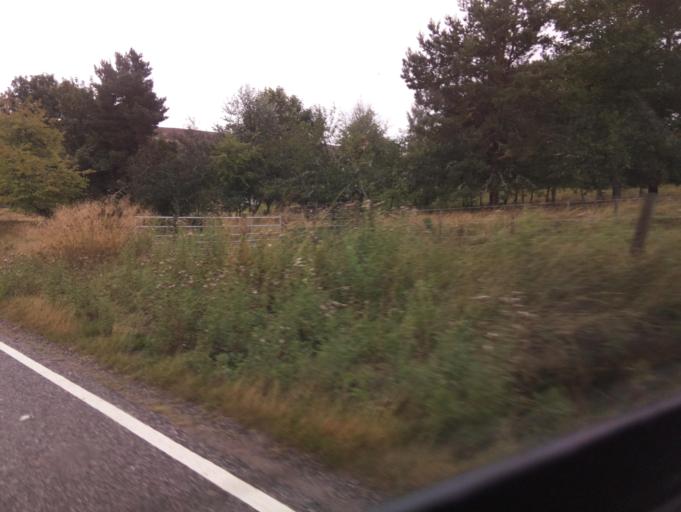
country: GB
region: Scotland
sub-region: Highland
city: Grantown on Spey
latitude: 57.2706
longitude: -3.4244
